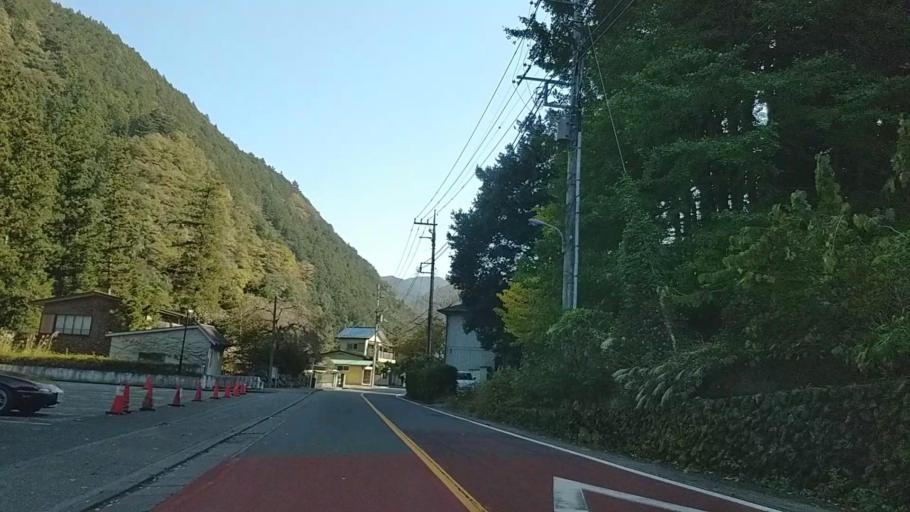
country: JP
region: Tokyo
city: Itsukaichi
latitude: 35.8067
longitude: 139.0989
